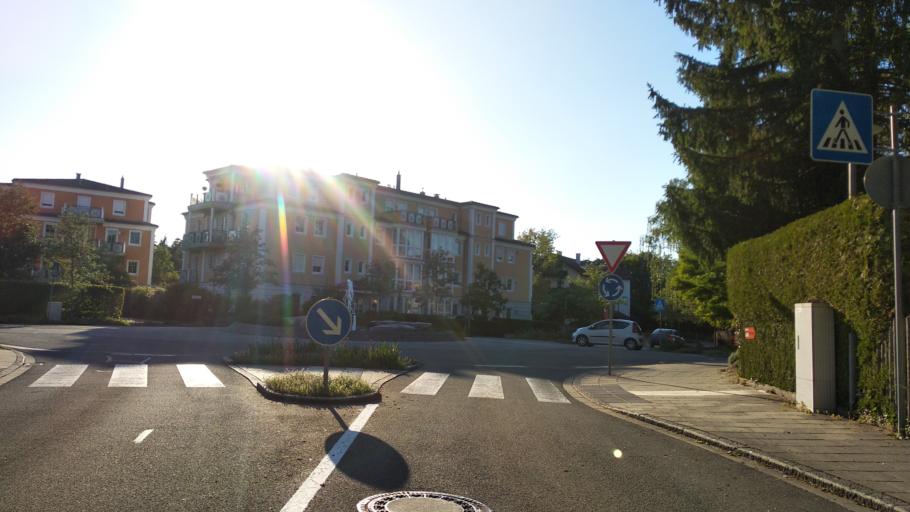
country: DE
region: Bavaria
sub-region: Upper Bavaria
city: Vaterstetten
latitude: 48.1015
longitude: 11.7889
